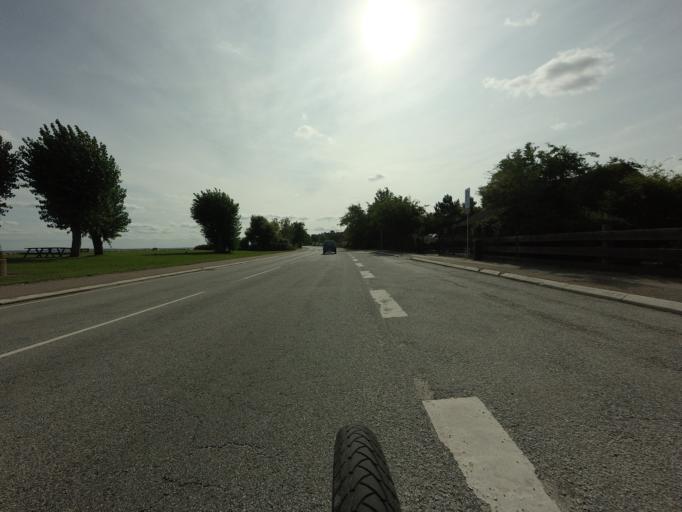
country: DK
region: Zealand
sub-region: Faxe Kommune
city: Fakse Ladeplads
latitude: 55.2094
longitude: 12.1519
